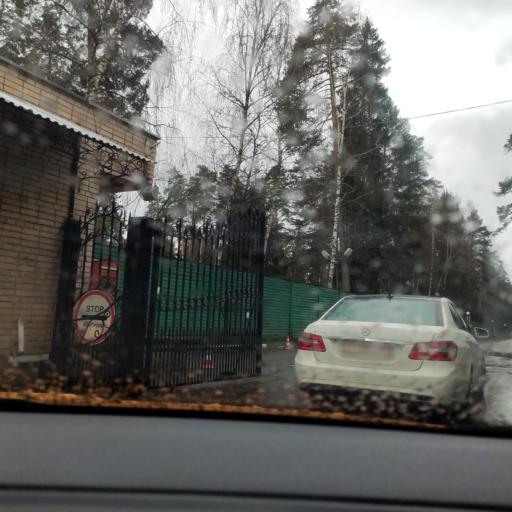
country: RU
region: Moskovskaya
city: Nikolina Gora
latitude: 55.7233
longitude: 36.9651
